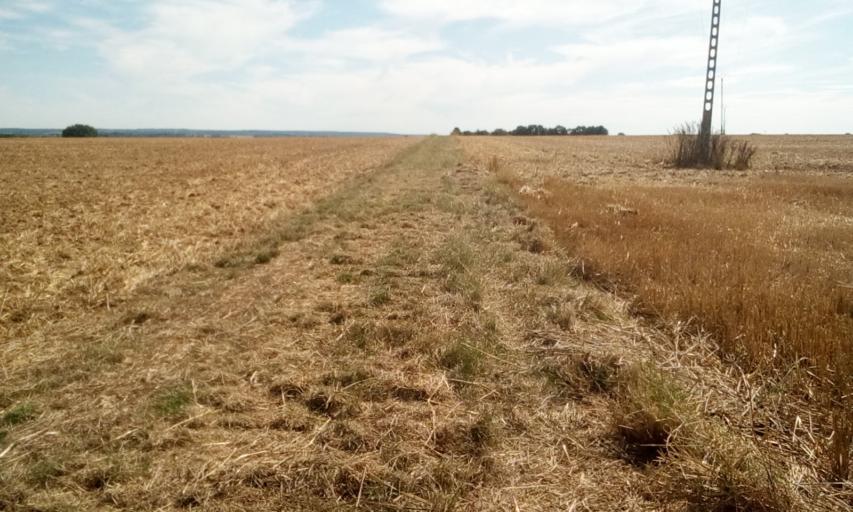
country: FR
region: Lower Normandy
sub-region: Departement du Calvados
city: Eterville
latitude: 49.1185
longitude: -0.4317
